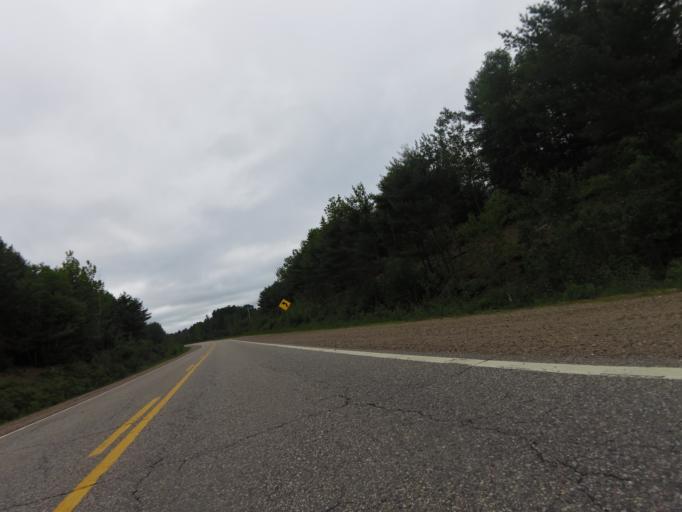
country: CA
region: Quebec
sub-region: Outaouais
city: Shawville
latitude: 45.8742
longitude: -76.4027
